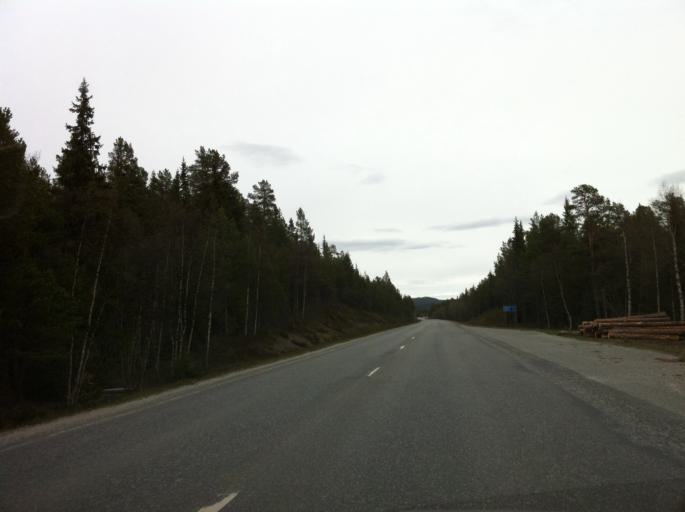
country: NO
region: Hedmark
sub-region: Engerdal
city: Engerdal
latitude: 62.5329
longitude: 12.5625
